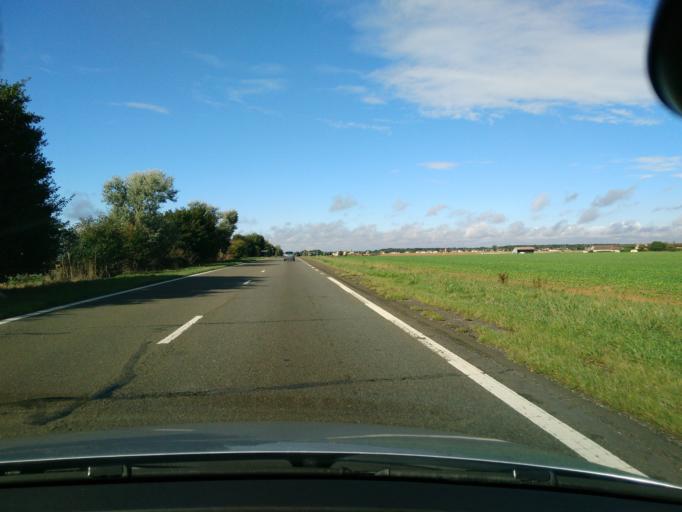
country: FR
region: Centre
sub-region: Departement d'Eure-et-Loir
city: Vert-en-Drouais
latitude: 48.7428
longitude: 1.2979
